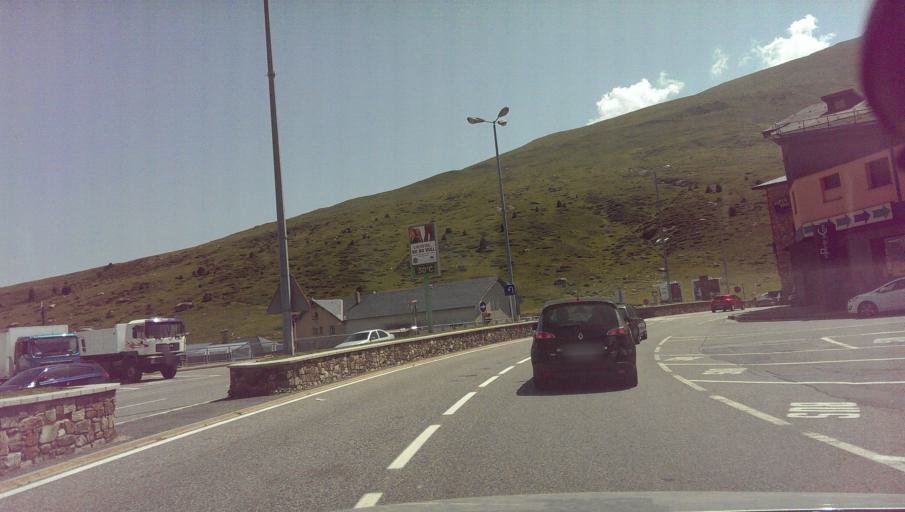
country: AD
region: Encamp
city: Pas de la Casa
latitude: 42.5437
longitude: 1.7345
